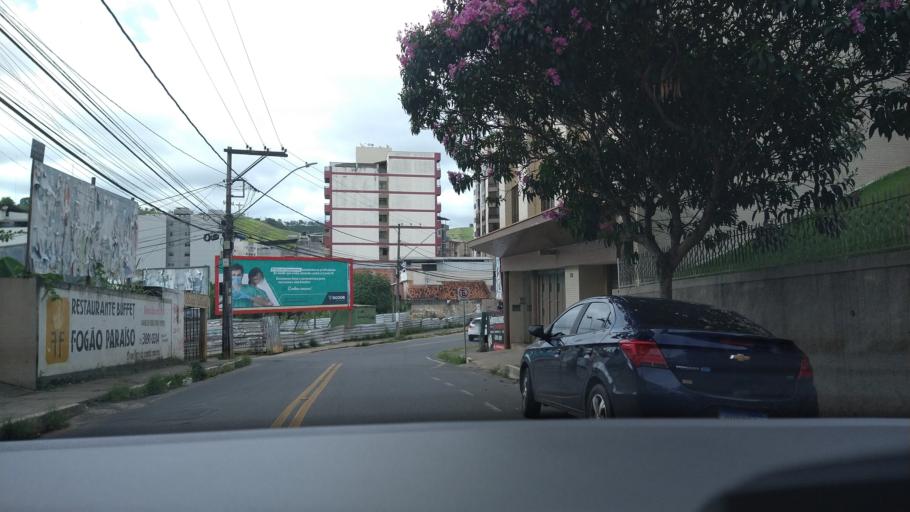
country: BR
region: Minas Gerais
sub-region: Vicosa
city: Vicosa
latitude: -20.7587
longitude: -42.8806
